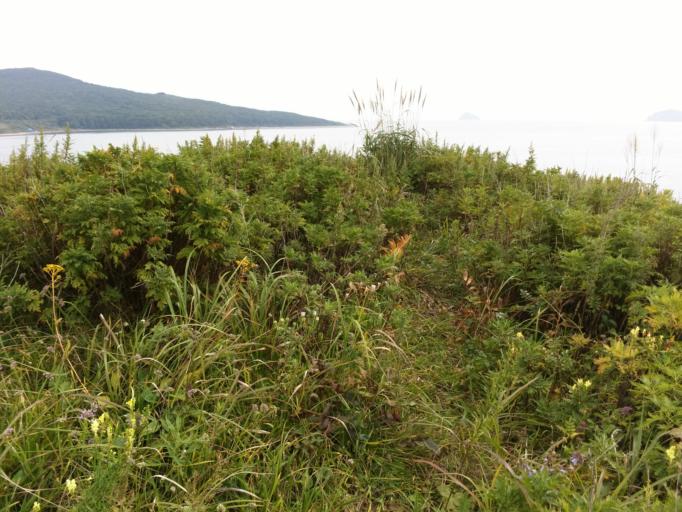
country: RU
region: Primorskiy
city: Popova
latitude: 42.9197
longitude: 131.7122
